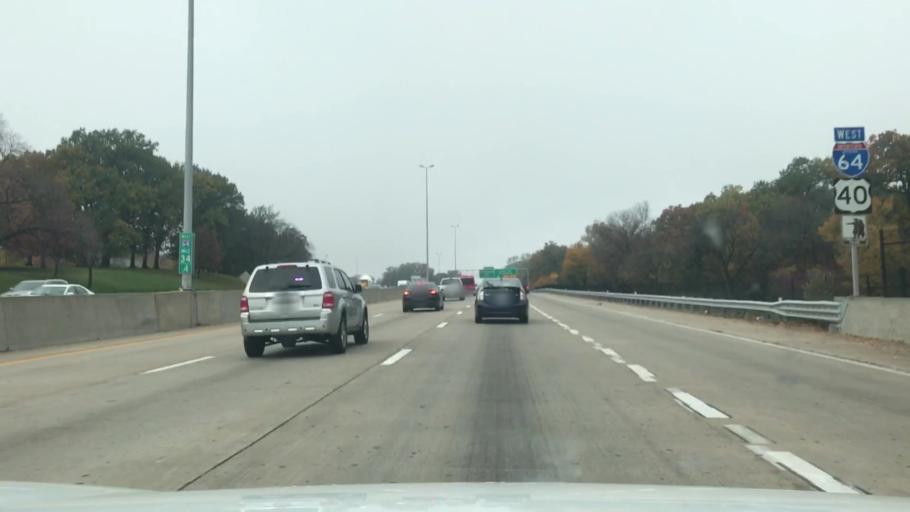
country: US
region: Missouri
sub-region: Saint Louis County
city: Richmond Heights
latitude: 38.6326
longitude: -90.2952
